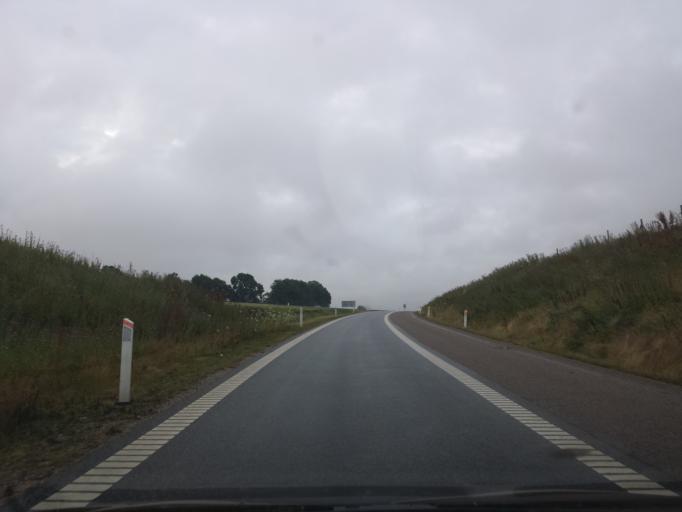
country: DK
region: South Denmark
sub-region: Sonderborg Kommune
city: Grasten
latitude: 54.9505
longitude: 9.6399
